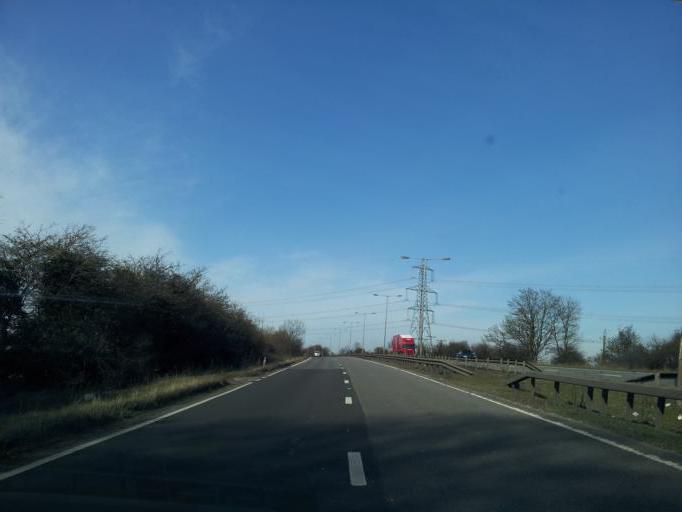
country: GB
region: England
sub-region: Lincolnshire
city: Grantham
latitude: 52.8686
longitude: -0.6299
